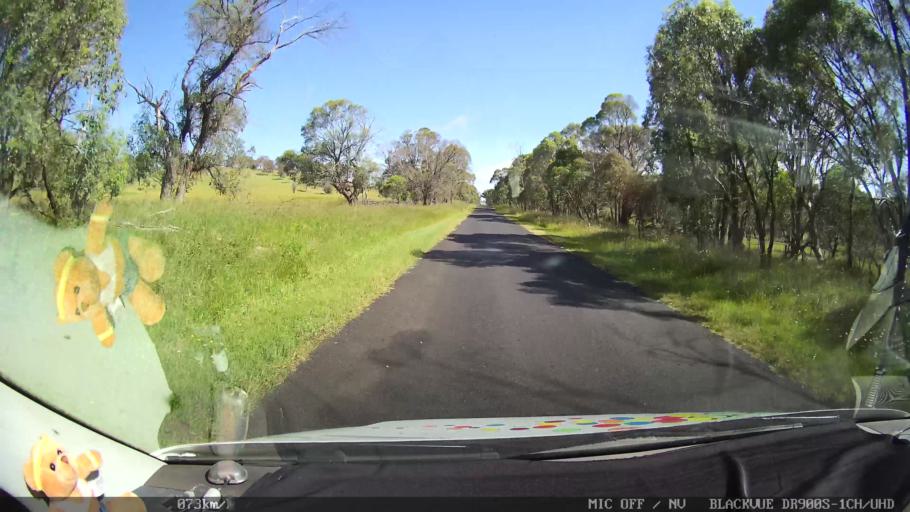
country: AU
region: New South Wales
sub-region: Guyra
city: Guyra
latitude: -30.0922
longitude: 151.6786
